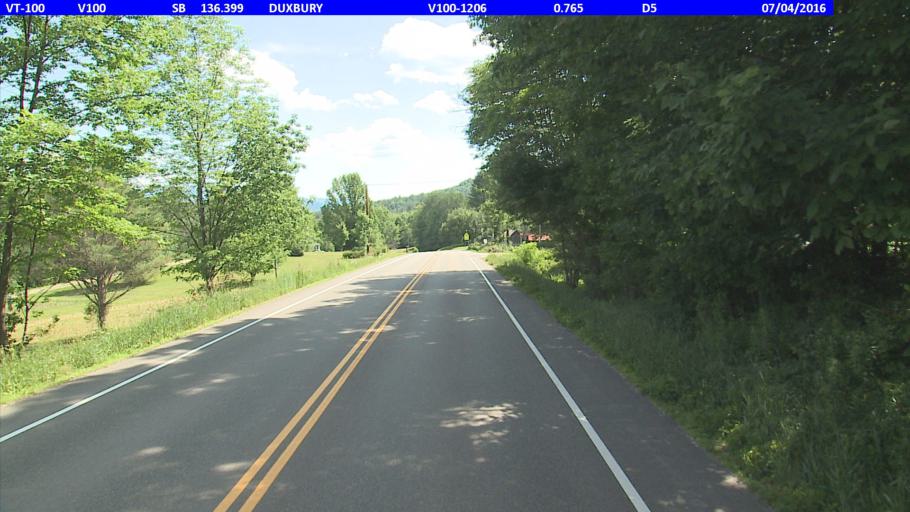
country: US
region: Vermont
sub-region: Washington County
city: Waterbury
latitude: 44.2574
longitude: -72.7885
